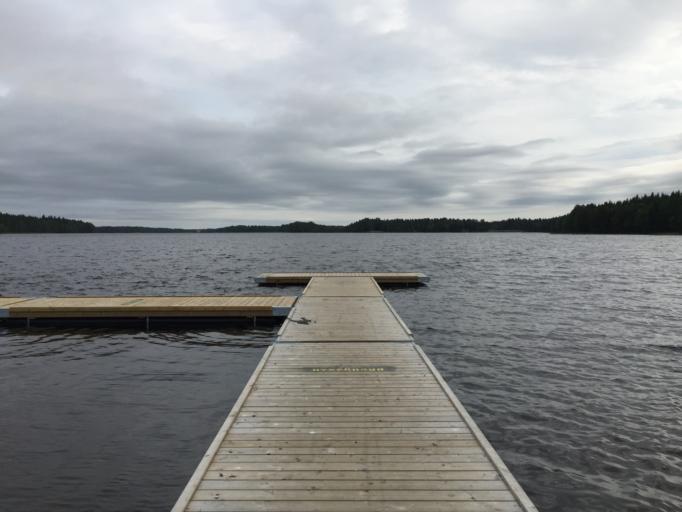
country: SE
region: Vaesterbotten
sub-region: Umea Kommun
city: Ersmark
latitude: 63.8361
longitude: 20.3399
